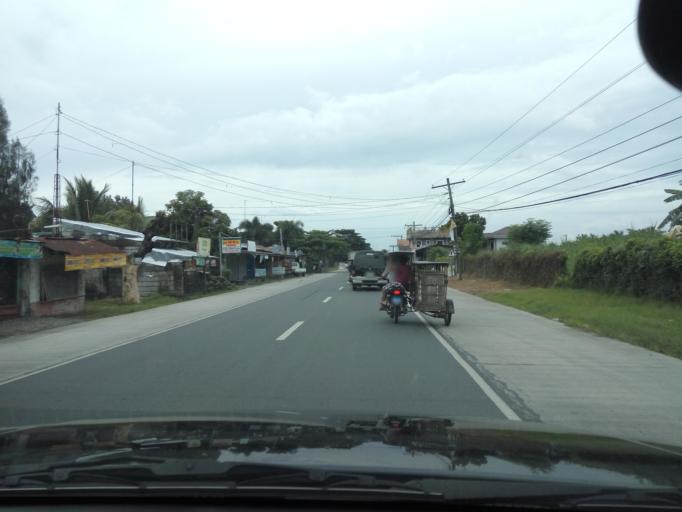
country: PH
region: Central Luzon
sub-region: Province of Nueva Ecija
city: Concepcion
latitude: 15.4482
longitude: 120.8079
